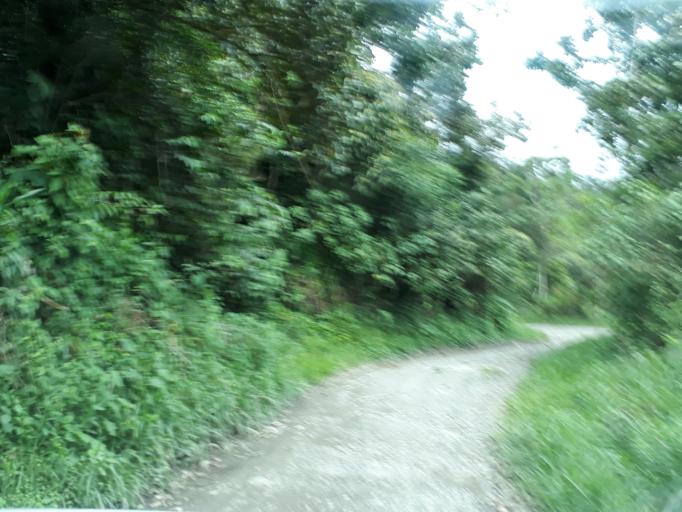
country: CO
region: Boyaca
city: Muzo
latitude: 5.3822
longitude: -74.0926
